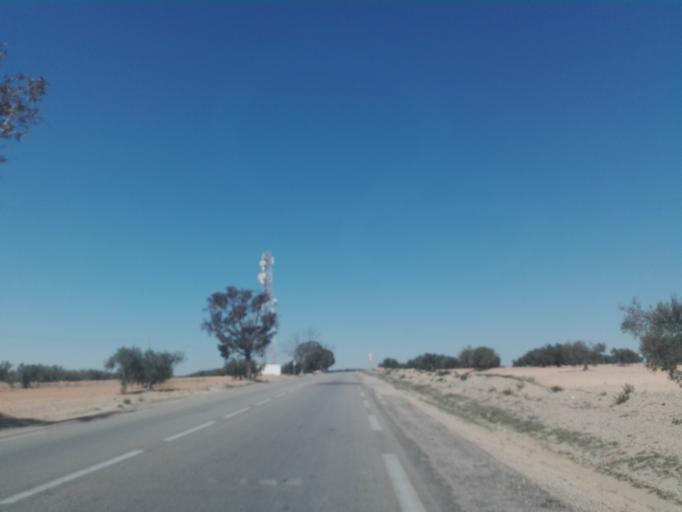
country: TN
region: Safaqis
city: Bi'r `Ali Bin Khalifah
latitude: 34.7555
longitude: 10.3312
